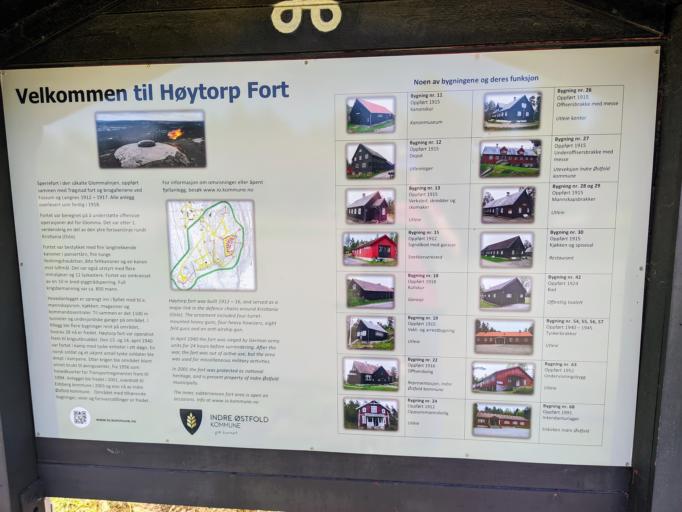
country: NO
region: Ostfold
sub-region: Eidsberg
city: Mysen
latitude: 59.5633
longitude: 11.3406
